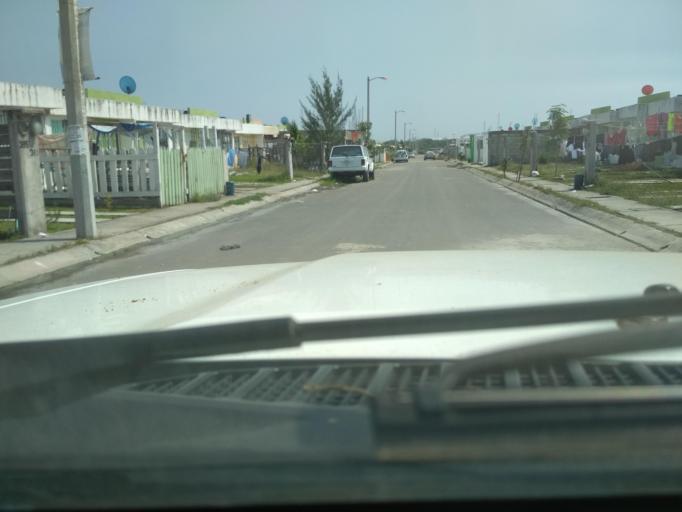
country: MX
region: Veracruz
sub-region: Veracruz
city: Lomas de Rio Medio Cuatro
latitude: 19.1874
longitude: -96.2106
